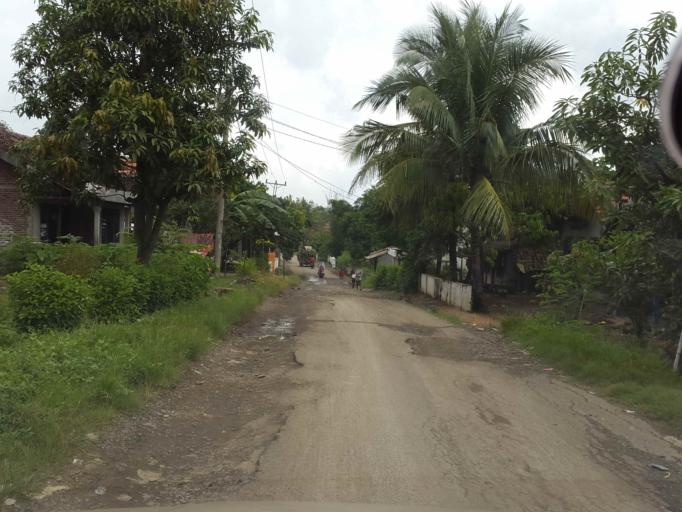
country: ID
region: Central Java
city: Pamedaran
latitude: -7.0333
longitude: 108.9405
